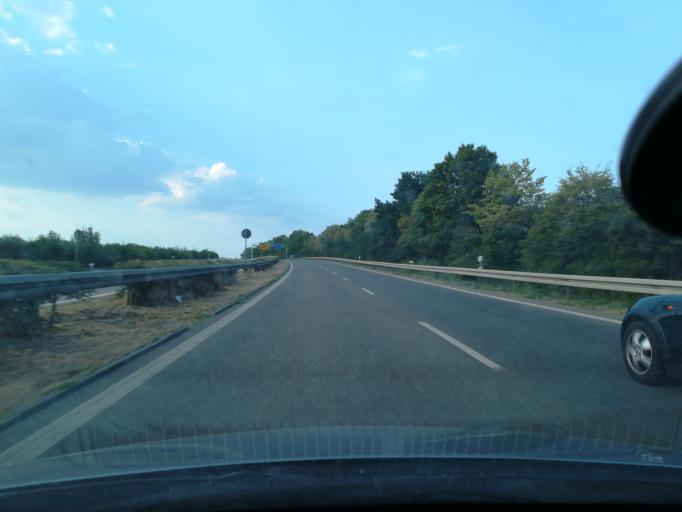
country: DE
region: Baden-Wuerttemberg
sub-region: Freiburg Region
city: Muhlhausen-Ehingen
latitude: 47.7876
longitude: 8.8297
